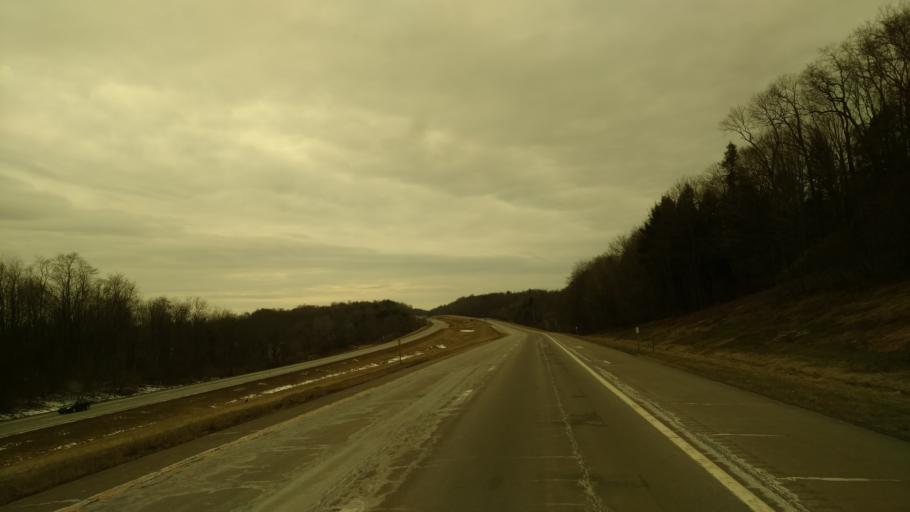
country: US
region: New York
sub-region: Chautauqua County
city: Celoron
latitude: 42.1275
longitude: -79.2867
